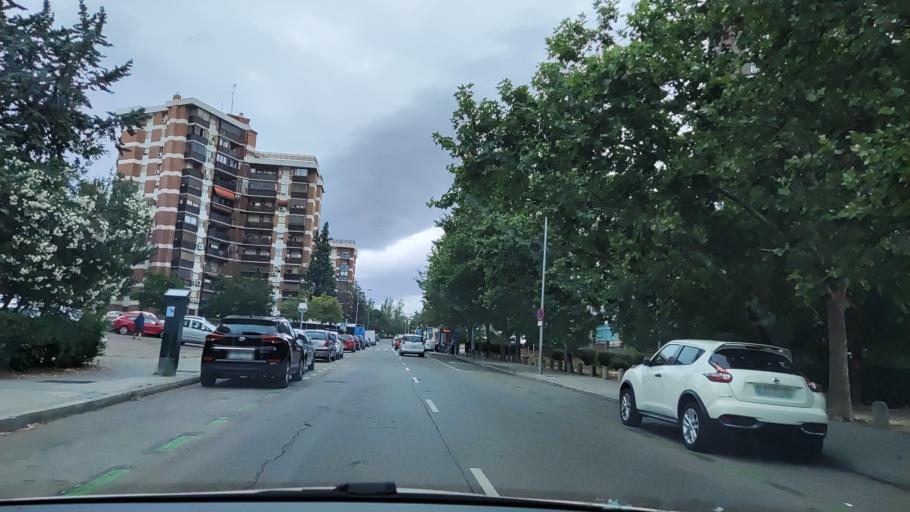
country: ES
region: Madrid
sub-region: Provincia de Madrid
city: Tetuan de las Victorias
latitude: 40.4864
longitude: -3.6983
